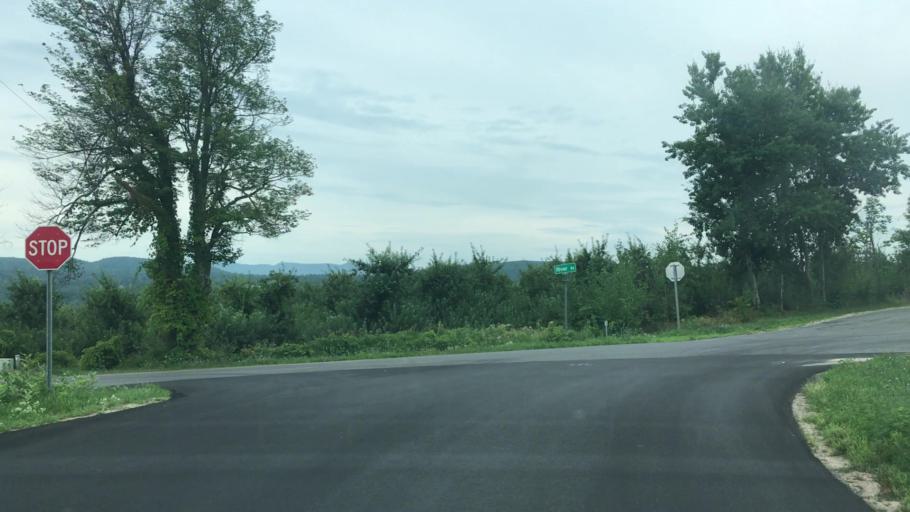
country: US
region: New York
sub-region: Clinton County
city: Peru
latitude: 44.5453
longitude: -73.5640
